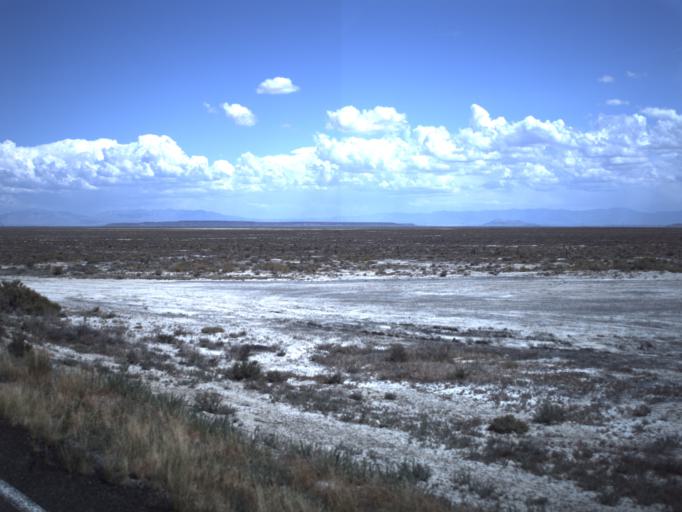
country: US
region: Utah
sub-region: Millard County
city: Delta
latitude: 39.1950
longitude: -112.9925
